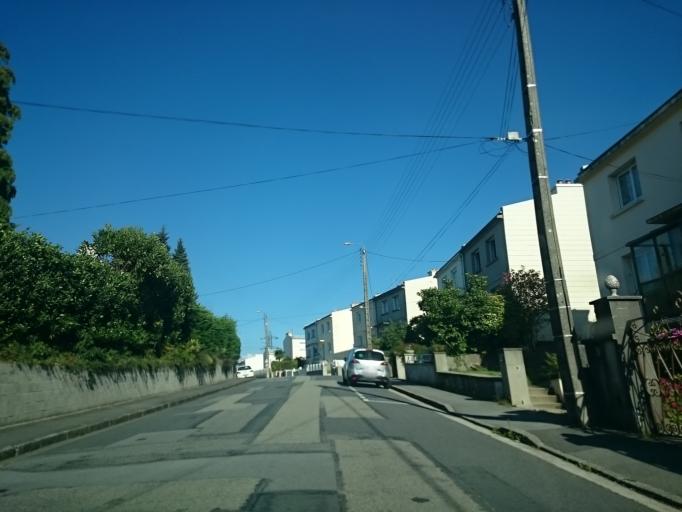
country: FR
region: Brittany
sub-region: Departement du Finistere
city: Gouesnou
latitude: 48.4247
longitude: -4.4637
